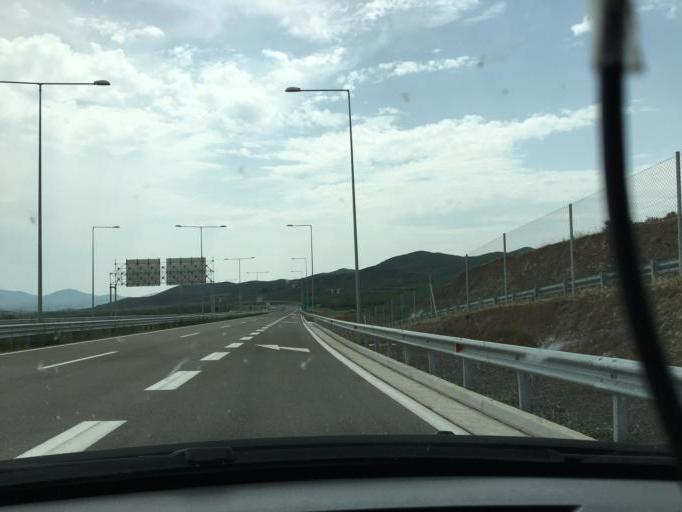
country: MK
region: Gevgelija
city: Miravci
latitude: 41.2951
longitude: 22.4328
